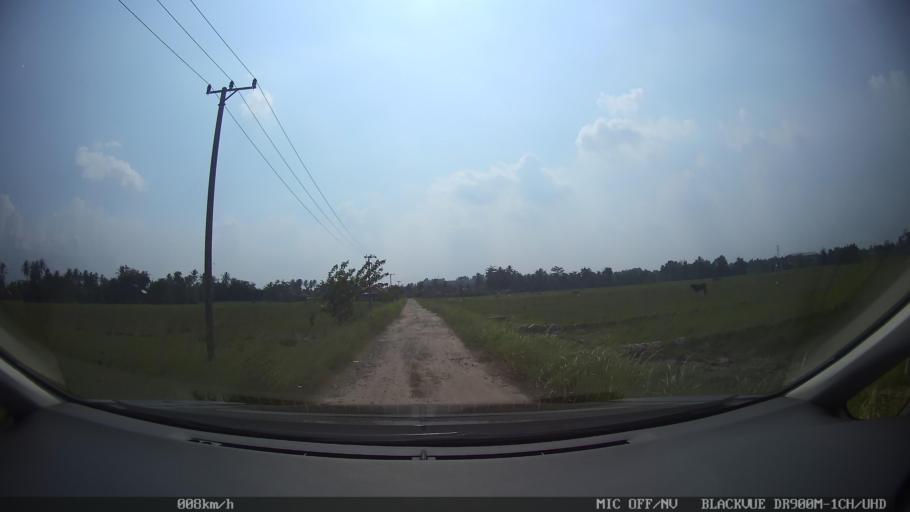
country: ID
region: Lampung
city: Natar
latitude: -5.2949
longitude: 105.2323
